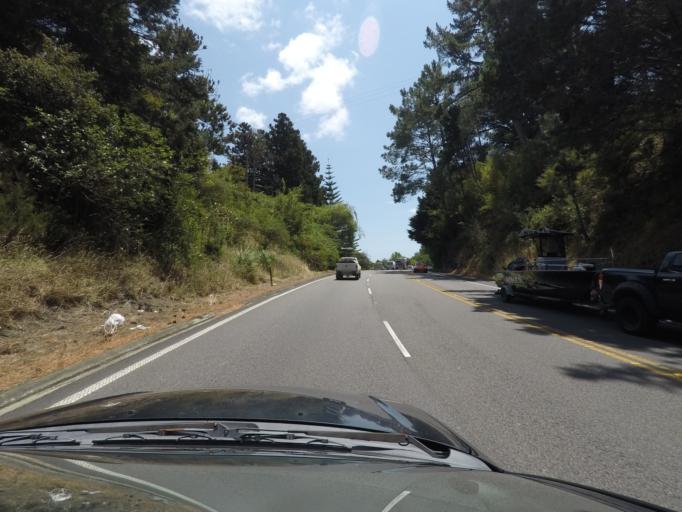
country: NZ
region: Auckland
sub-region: Auckland
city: Warkworth
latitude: -36.4278
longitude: 174.6464
